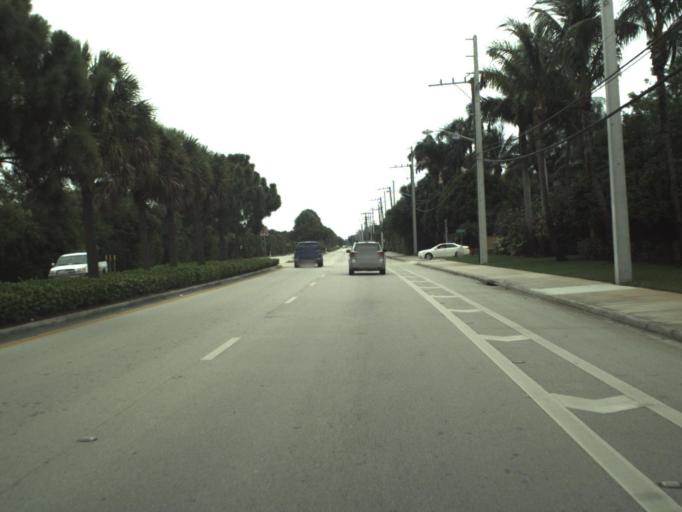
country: US
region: Florida
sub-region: Palm Beach County
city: Hypoluxo
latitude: 26.5618
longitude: -80.0539
